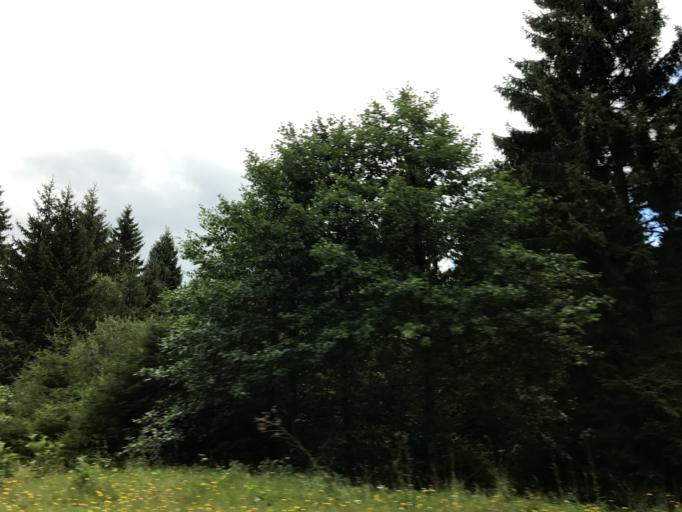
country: DE
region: Lower Saxony
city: Bad Harzburg
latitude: 51.8311
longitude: 10.5235
